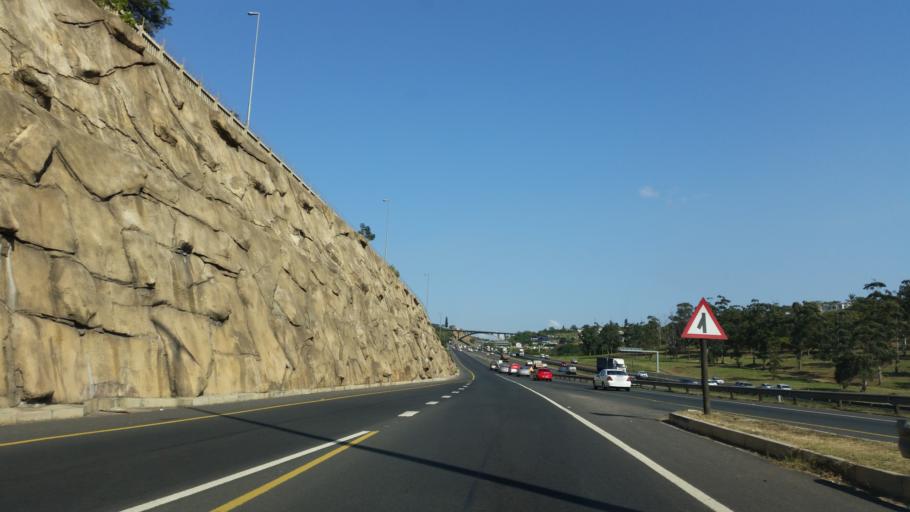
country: ZA
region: KwaZulu-Natal
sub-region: eThekwini Metropolitan Municipality
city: Berea
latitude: -29.8084
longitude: 30.9772
